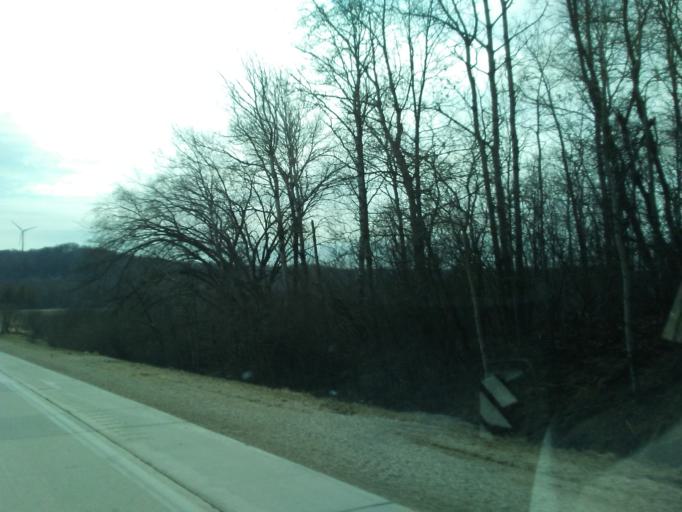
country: US
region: Iowa
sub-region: Winneshiek County
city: Decorah
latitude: 43.3254
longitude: -91.8133
